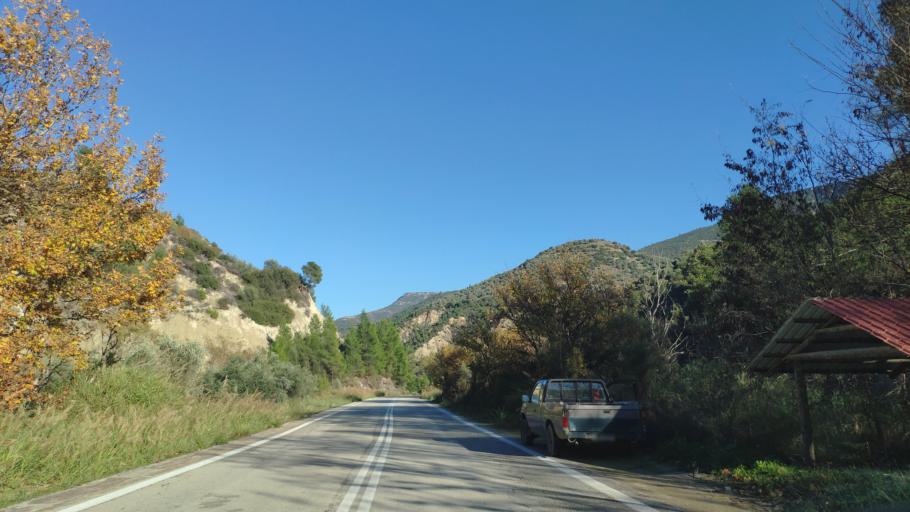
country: GR
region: Peloponnese
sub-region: Nomos Korinthias
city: Xylokastro
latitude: 38.0107
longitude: 22.5404
